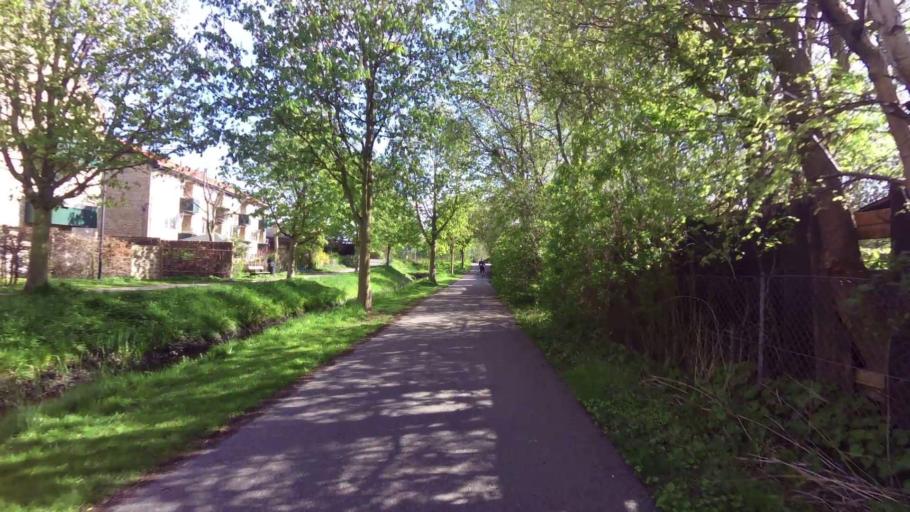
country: DK
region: Capital Region
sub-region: Lyngby-Tarbaek Kommune
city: Kongens Lyngby
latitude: 55.7380
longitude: 12.5342
